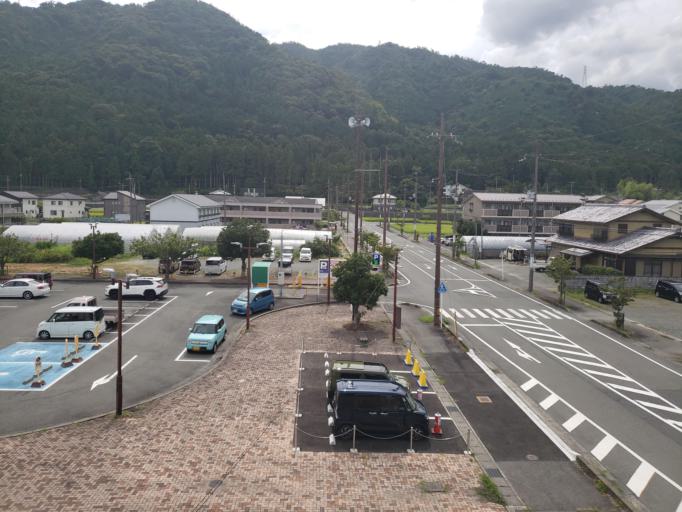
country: JP
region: Shiga Prefecture
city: Kitahama
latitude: 35.2928
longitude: 136.0100
